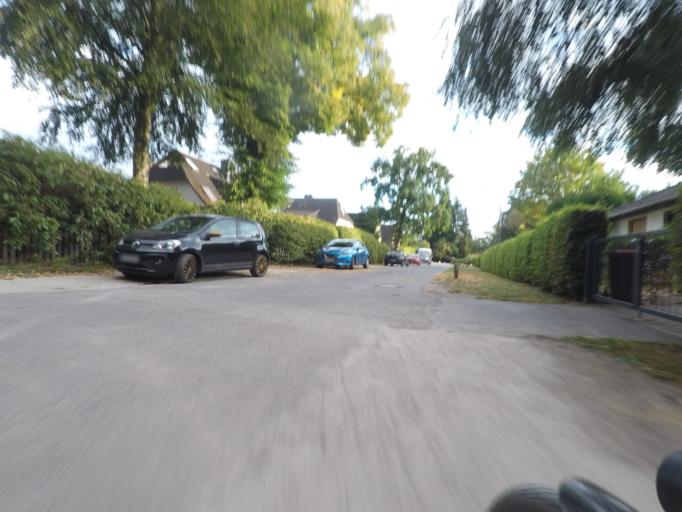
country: DE
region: Hamburg
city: Farmsen-Berne
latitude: 53.6228
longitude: 10.1028
